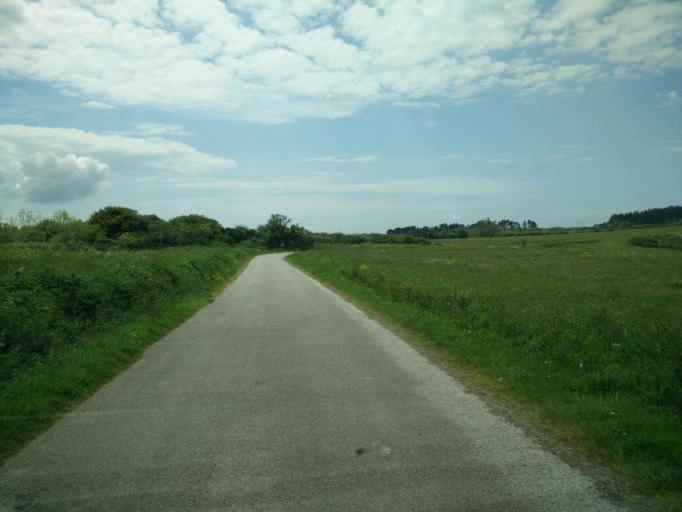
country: FR
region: Brittany
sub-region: Departement du Finistere
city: Roscanvel
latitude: 48.3366
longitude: -4.5442
